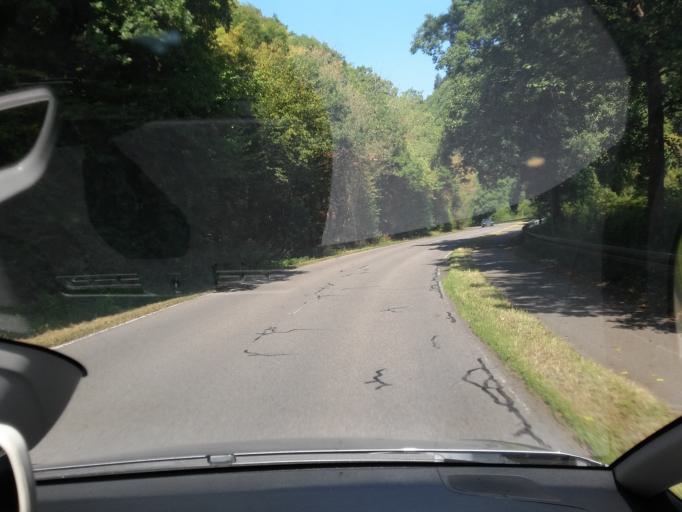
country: DE
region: Saarland
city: Mettlach
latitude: 49.4820
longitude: 6.5742
